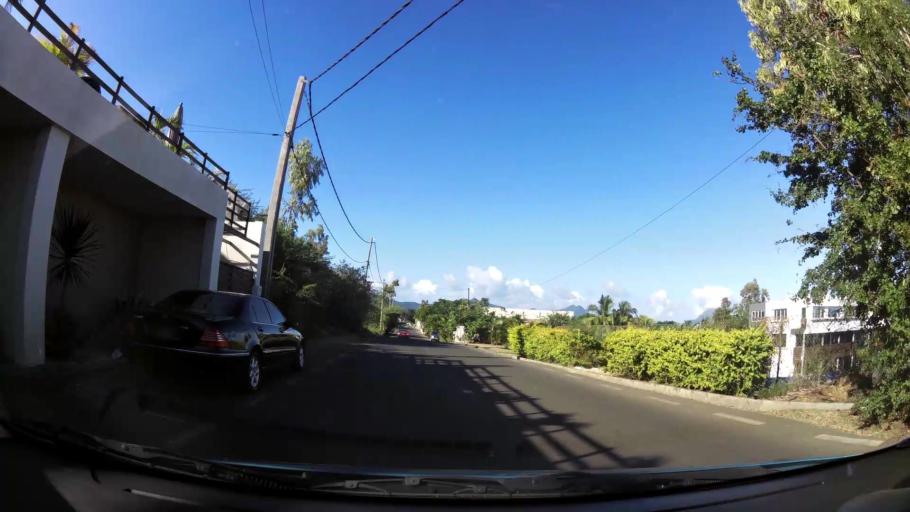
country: MU
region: Black River
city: Grande Riviere Noire
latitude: -20.3518
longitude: 57.3653
